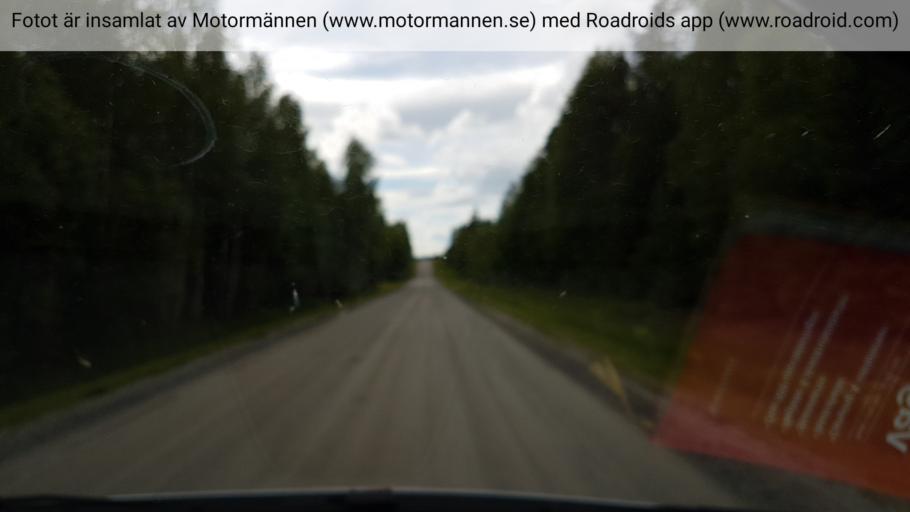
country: SE
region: Vaesternorrland
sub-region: Solleftea Kommun
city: Solleftea
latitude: 63.3357
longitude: 17.4359
